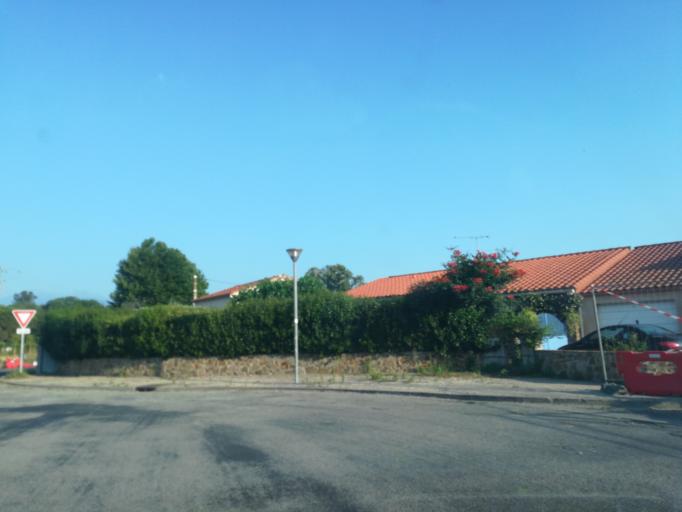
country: FR
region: Languedoc-Roussillon
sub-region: Departement des Pyrenees-Orientales
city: Maureillas-las-Illas
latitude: 42.4914
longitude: 2.7994
